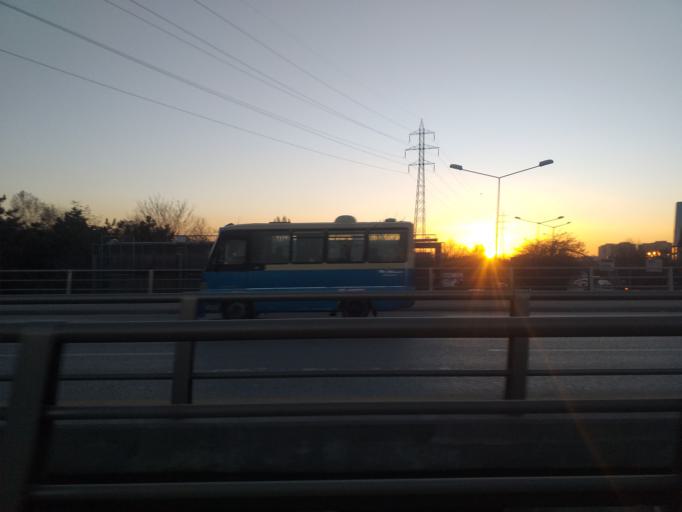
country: TR
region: Ankara
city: Ankara
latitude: 39.9547
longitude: 32.8202
